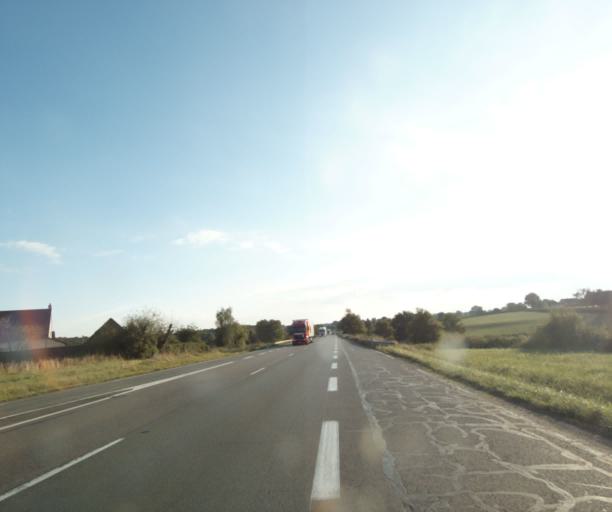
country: FR
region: Bourgogne
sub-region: Departement de Saone-et-Loire
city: Palinges
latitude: 46.5588
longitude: 4.1866
